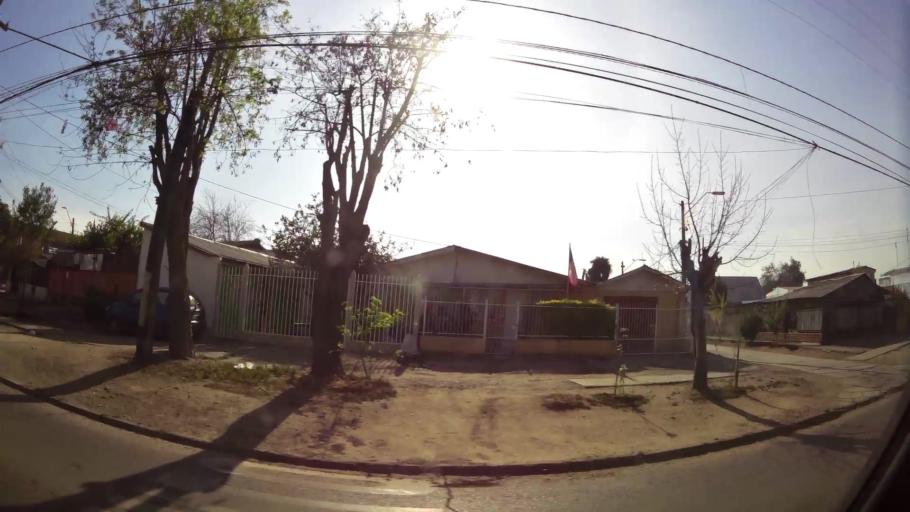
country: CL
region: Santiago Metropolitan
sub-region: Provincia de Santiago
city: Lo Prado
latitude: -33.4175
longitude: -70.7574
